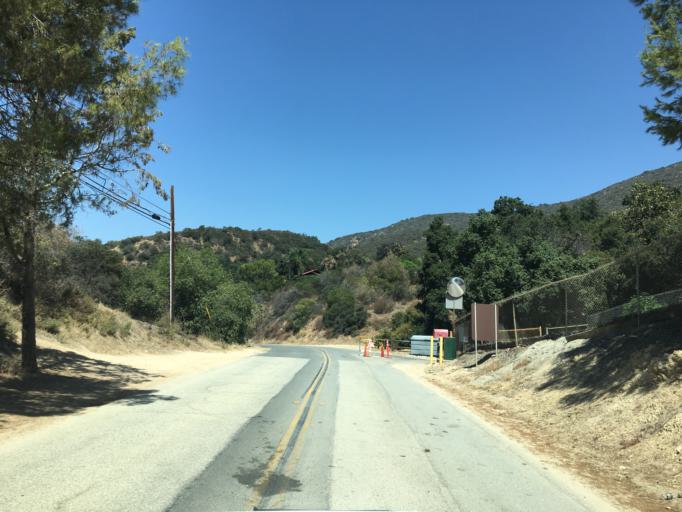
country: US
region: California
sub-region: Los Angeles County
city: La Verne
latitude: 34.1524
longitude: -117.7460
